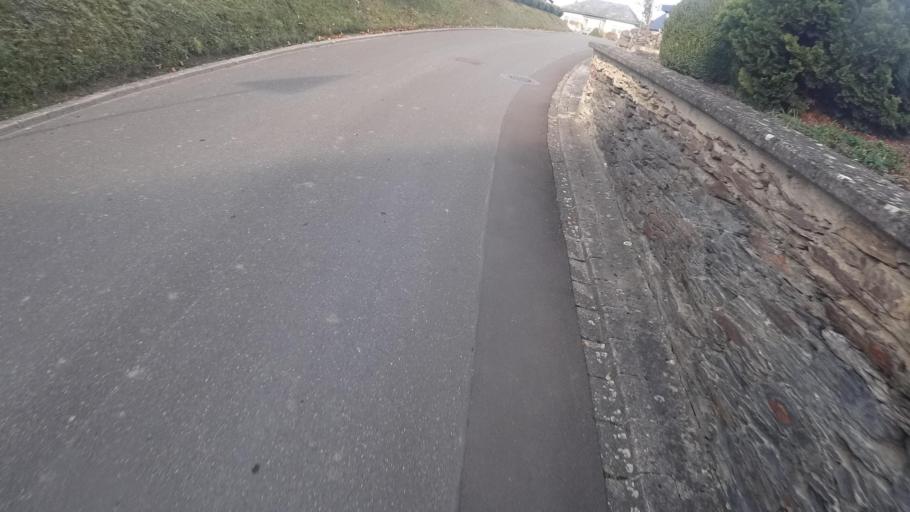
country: DE
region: Rheinland-Pfalz
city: Muhlpfad
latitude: 50.1214
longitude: 7.5548
